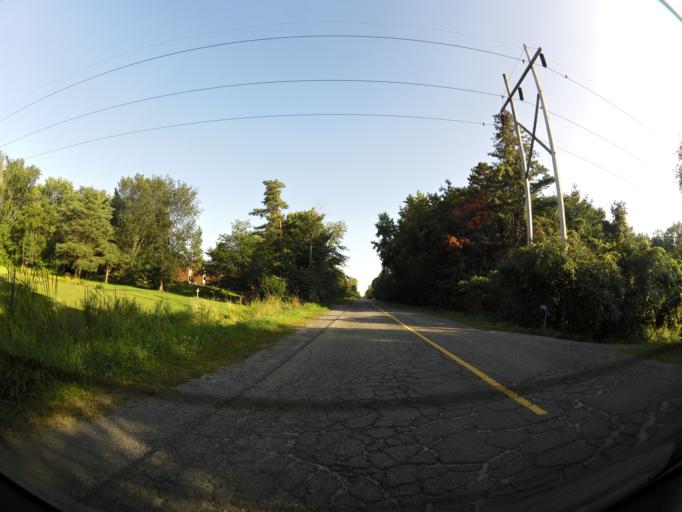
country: CA
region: Ontario
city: Clarence-Rockland
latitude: 45.5102
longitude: -75.4609
